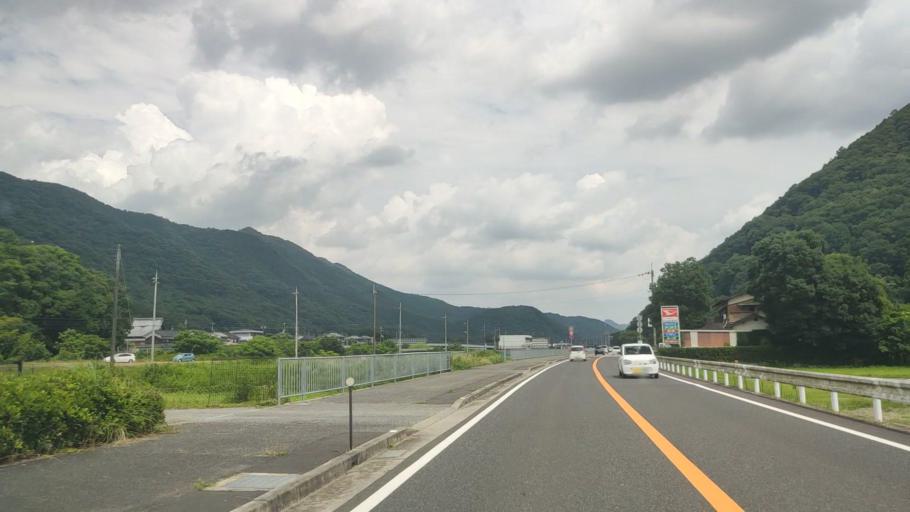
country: JP
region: Hyogo
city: Yamazakicho-nakabirose
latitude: 34.9398
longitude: 134.5057
